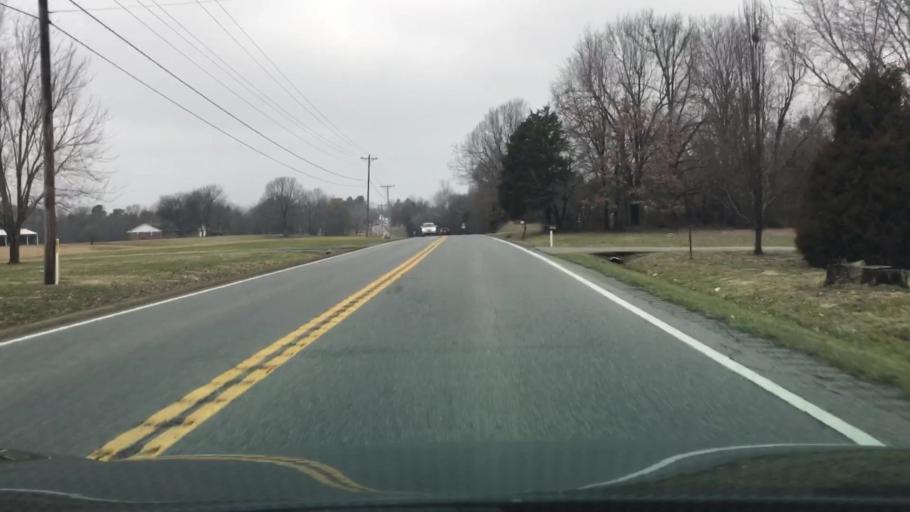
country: US
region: Kentucky
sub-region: Marshall County
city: Calvert City
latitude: 36.9547
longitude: -88.3714
